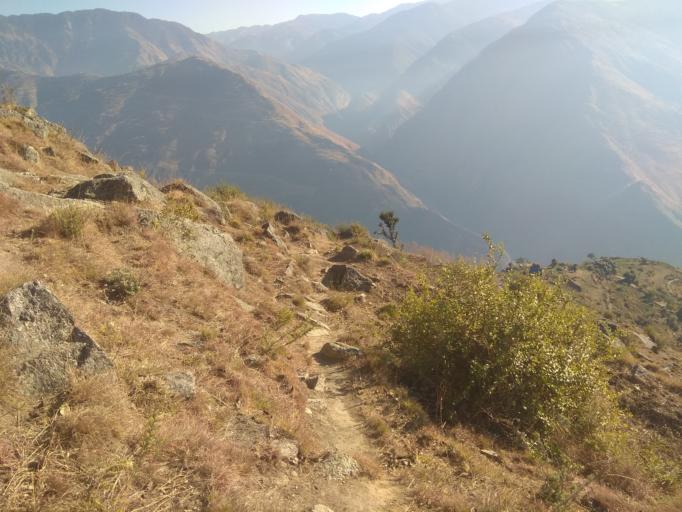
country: NP
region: Mid Western
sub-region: Karnali Zone
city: Jumla
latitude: 29.3139
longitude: 81.7367
